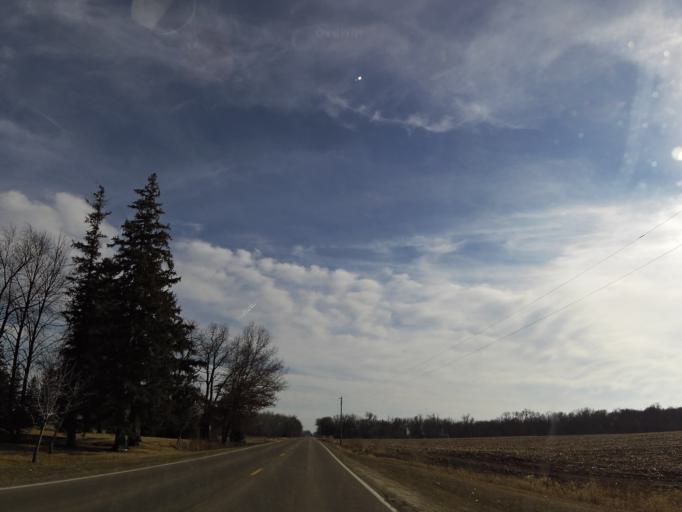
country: US
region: Minnesota
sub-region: Rice County
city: Northfield
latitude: 44.5211
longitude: -93.2005
